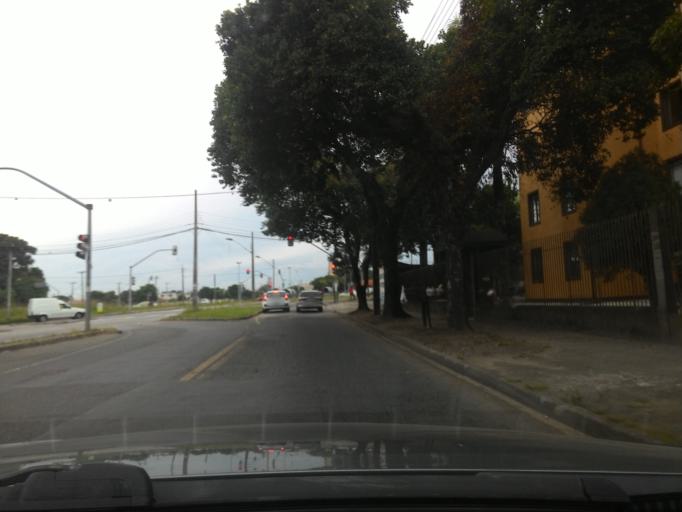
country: BR
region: Parana
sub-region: Pinhais
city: Pinhais
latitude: -25.4437
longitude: -49.2079
